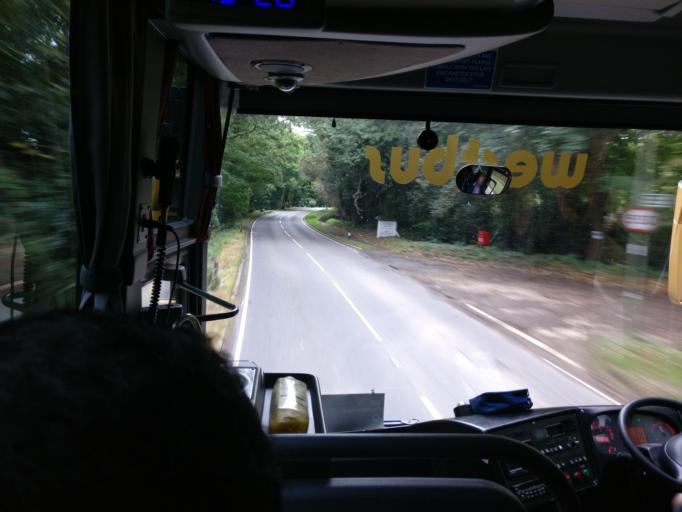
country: GB
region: England
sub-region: Surrey
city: Chobham
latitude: 51.3406
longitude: -0.5888
